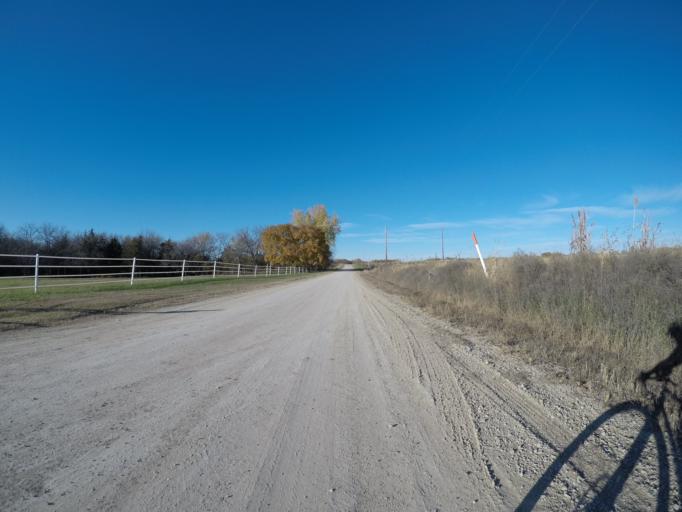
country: US
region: Kansas
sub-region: Riley County
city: Fort Riley North
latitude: 39.2689
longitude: -96.7844
